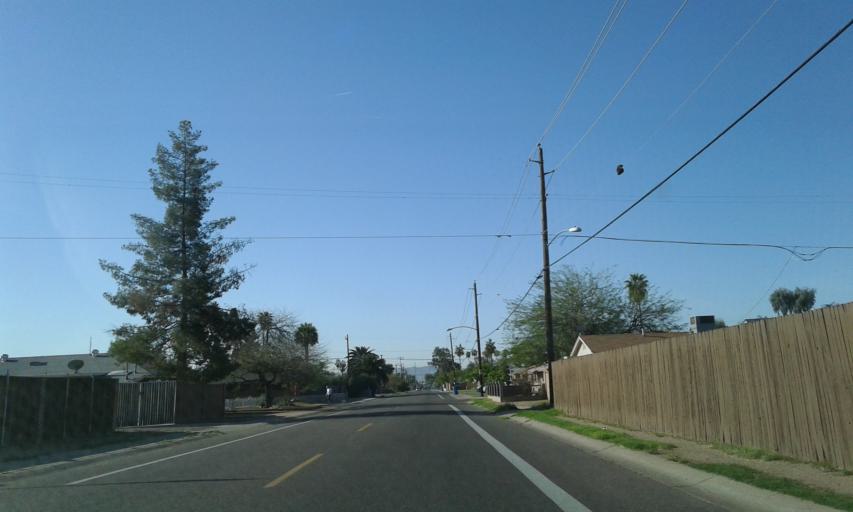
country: US
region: Arizona
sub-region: Maricopa County
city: Phoenix
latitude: 33.4854
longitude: -112.1085
